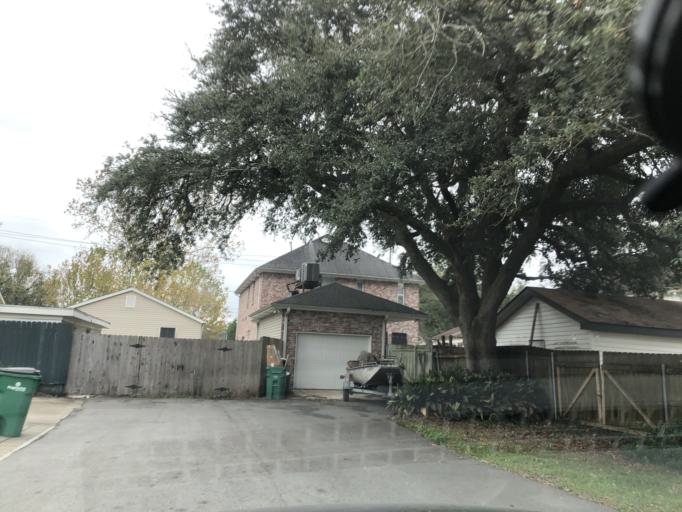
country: US
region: Louisiana
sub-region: Jefferson Parish
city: Metairie
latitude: 29.9900
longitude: -90.1532
